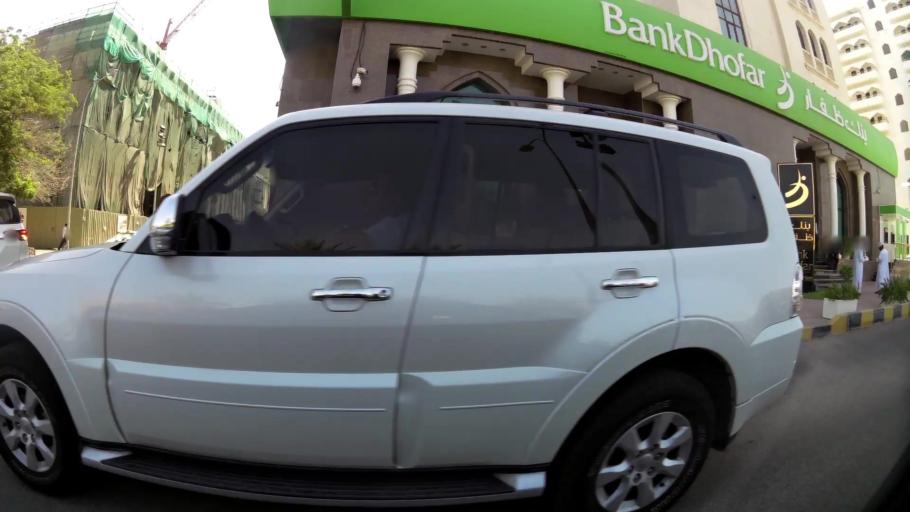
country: OM
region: Muhafazat Masqat
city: Muscat
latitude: 23.5993
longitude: 58.5465
